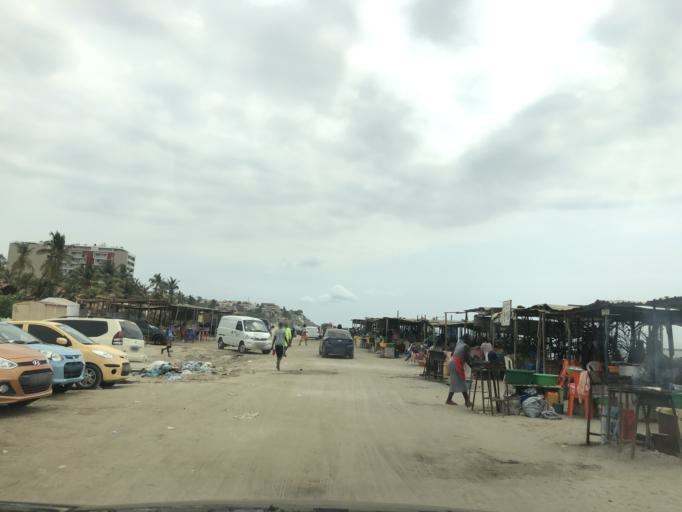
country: AO
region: Luanda
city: Luanda
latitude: -8.8743
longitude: 13.1910
